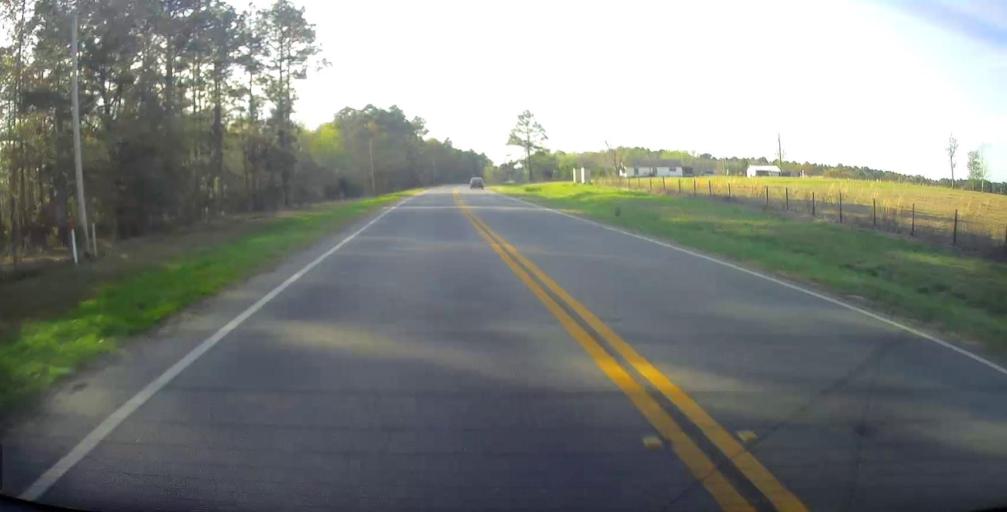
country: US
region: Georgia
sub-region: Toombs County
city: Lyons
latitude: 32.1757
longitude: -82.2835
